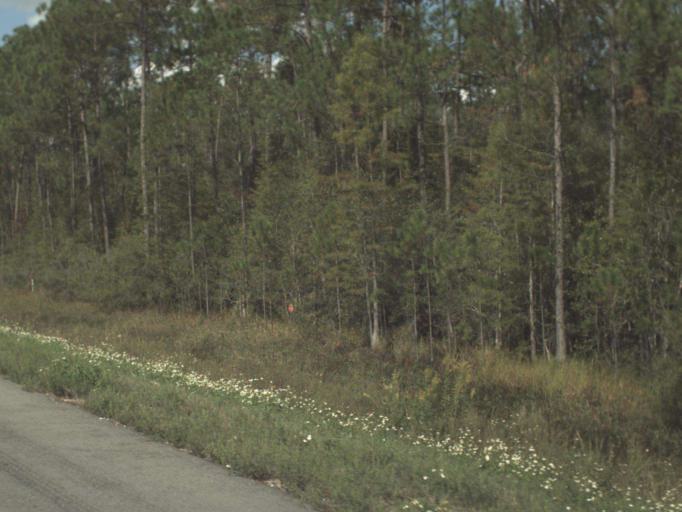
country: US
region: Florida
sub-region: Bay County
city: Laguna Beach
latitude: 30.4580
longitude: -85.9193
